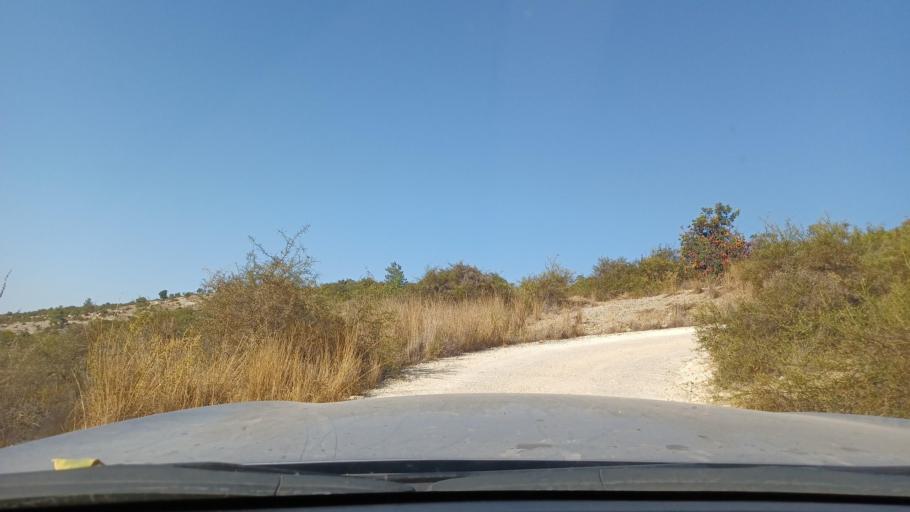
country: CY
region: Pafos
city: Polis
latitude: 35.0036
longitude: 32.4898
